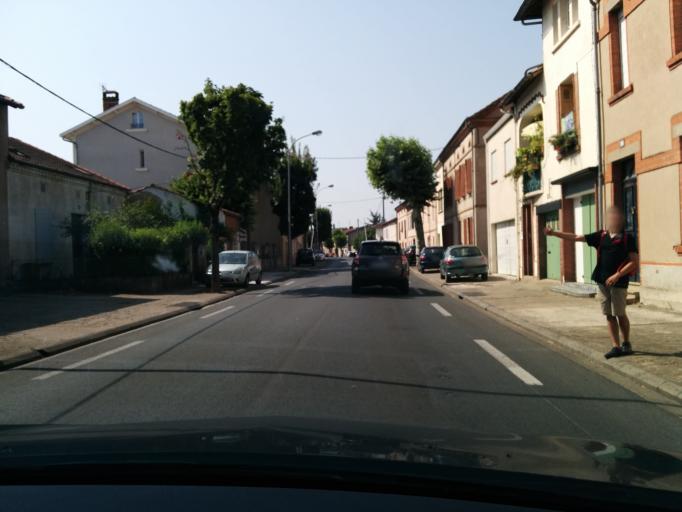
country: FR
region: Midi-Pyrenees
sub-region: Departement du Tarn
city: Albi
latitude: 43.9393
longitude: 2.1416
